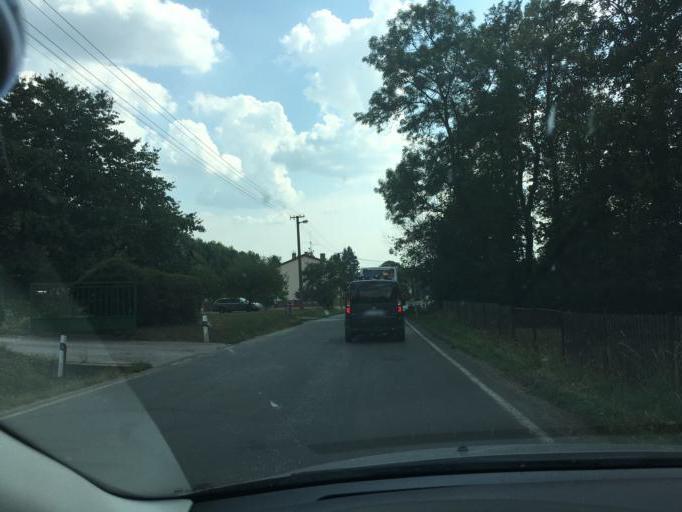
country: CZ
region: Kralovehradecky
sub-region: Okres Trutnov
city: Rudnik
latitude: 50.6123
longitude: 15.7070
